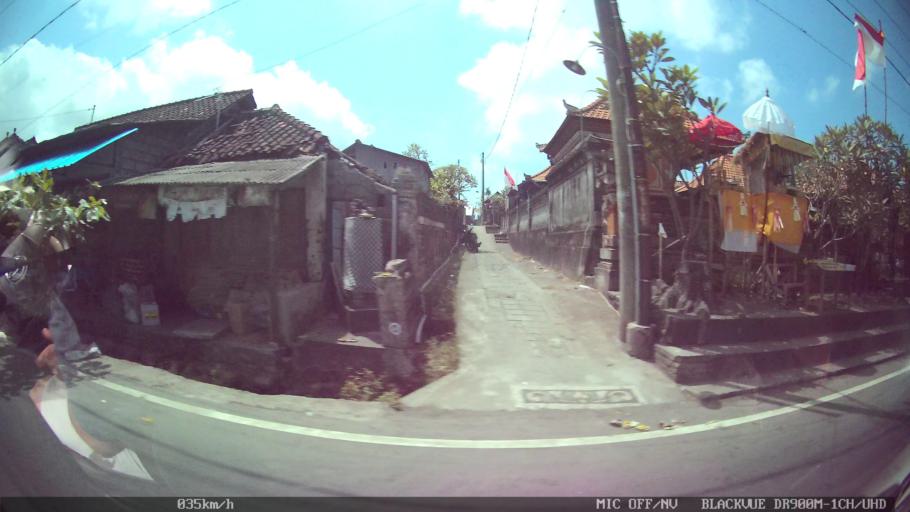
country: ID
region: Bali
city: Banjar Pasekan
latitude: -8.5992
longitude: 115.3008
